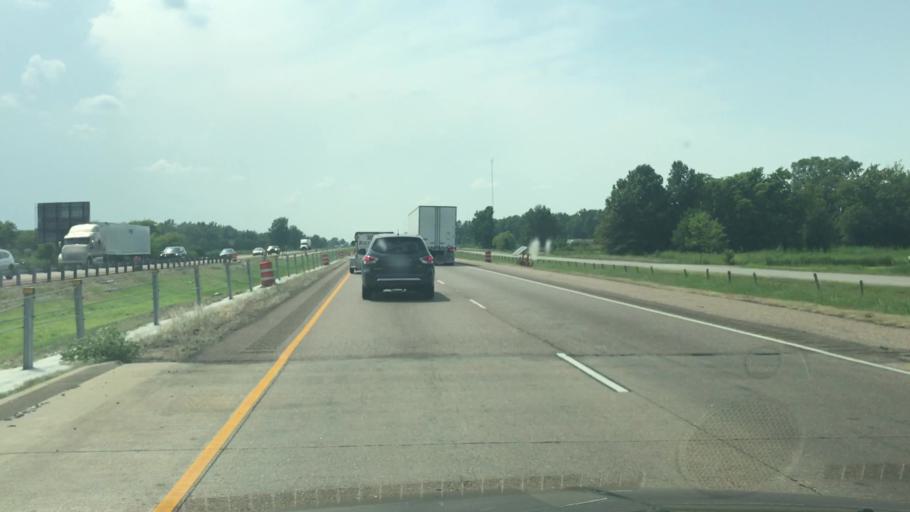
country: US
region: Arkansas
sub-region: Crittenden County
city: Earle
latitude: 35.1504
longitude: -90.3728
